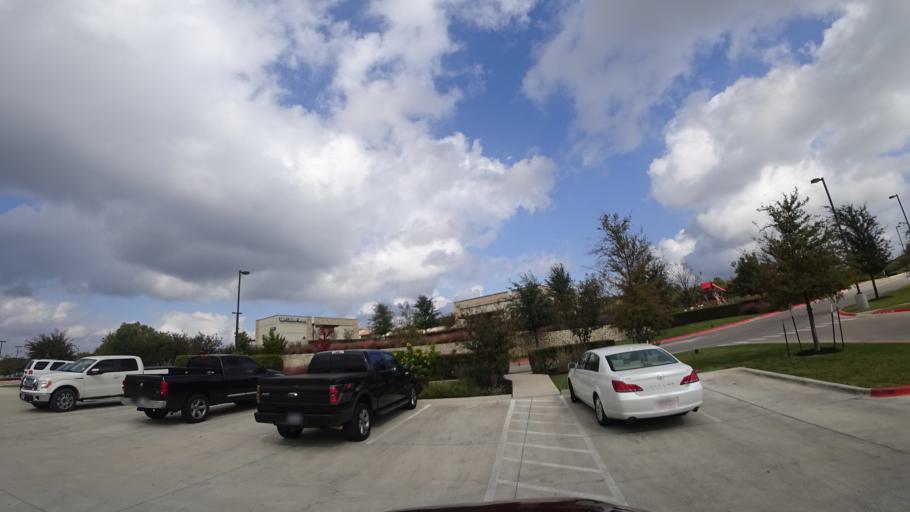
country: US
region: Texas
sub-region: Travis County
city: Hudson Bend
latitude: 30.3874
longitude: -97.8839
